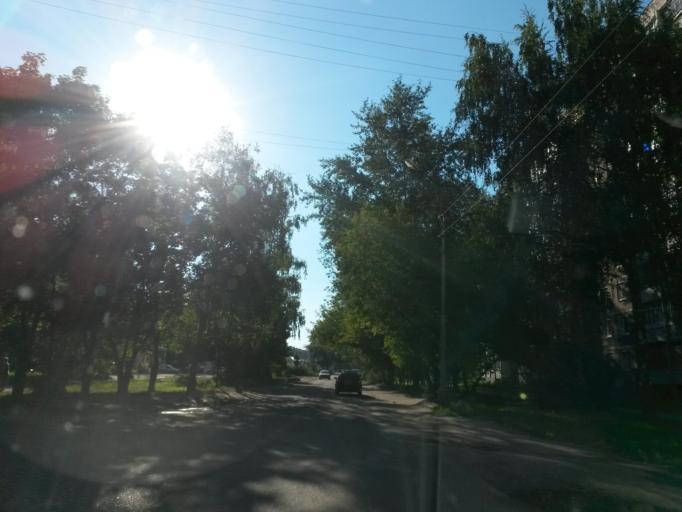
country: RU
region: Ivanovo
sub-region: Gorod Ivanovo
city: Ivanovo
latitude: 56.9825
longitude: 40.9730
